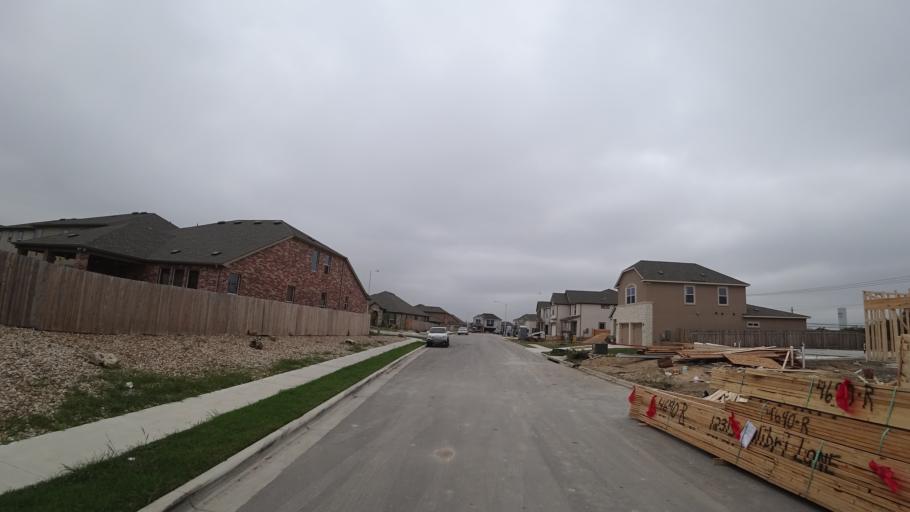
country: US
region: Texas
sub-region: Travis County
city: Pflugerville
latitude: 30.3912
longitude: -97.6472
